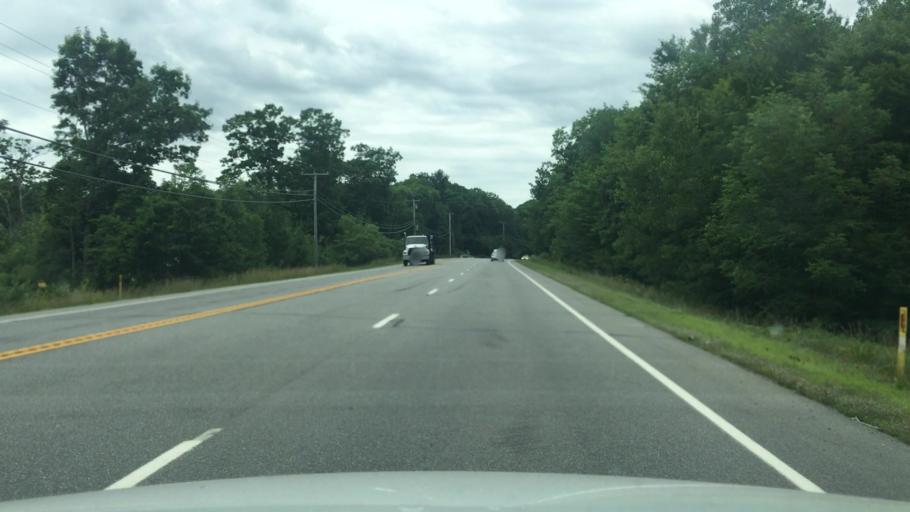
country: US
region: Maine
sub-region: Kennebec County
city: Sidney
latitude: 44.3371
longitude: -69.6741
